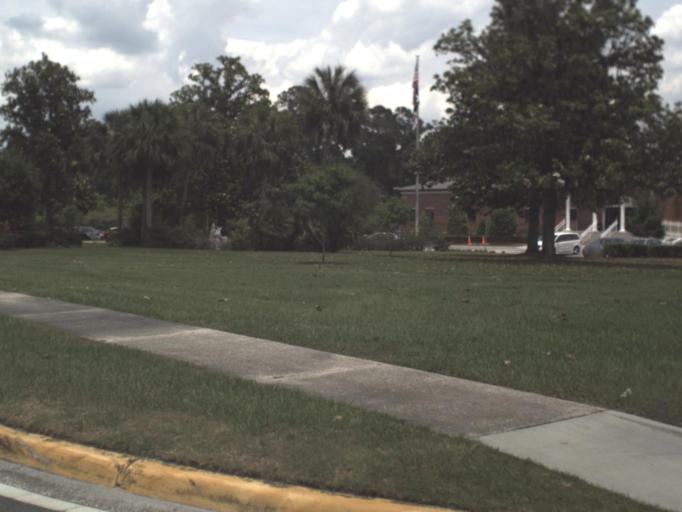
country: US
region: Florida
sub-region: Columbia County
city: Lake City
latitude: 30.1742
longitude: -82.6369
